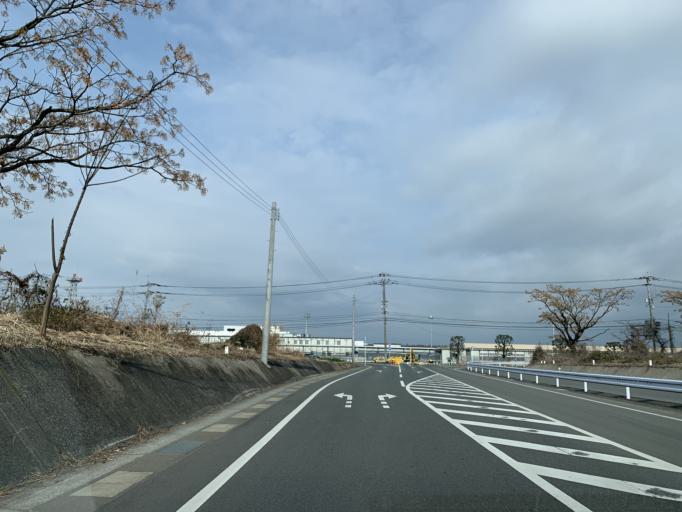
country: JP
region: Kumamoto
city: Ozu
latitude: 32.8337
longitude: 130.8628
